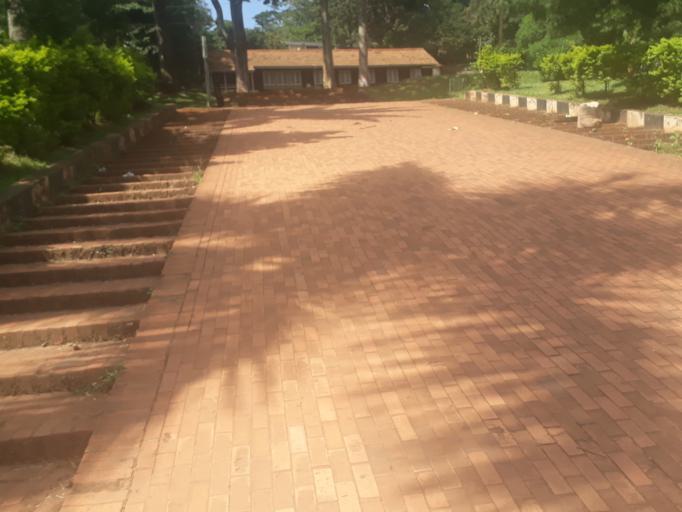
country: UG
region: Central Region
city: Kampala Central Division
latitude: 0.3318
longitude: 32.5662
